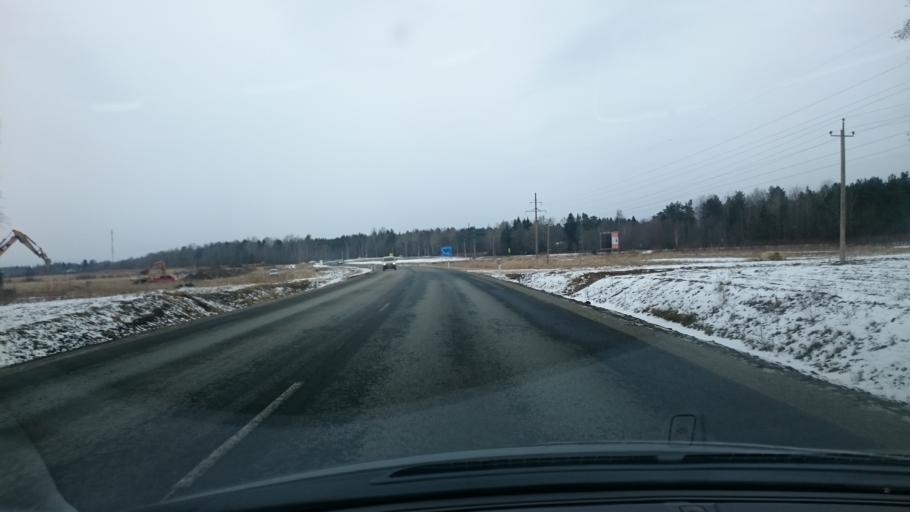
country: EE
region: Harju
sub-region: Saue vald
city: Laagri
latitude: 59.3568
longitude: 24.6006
